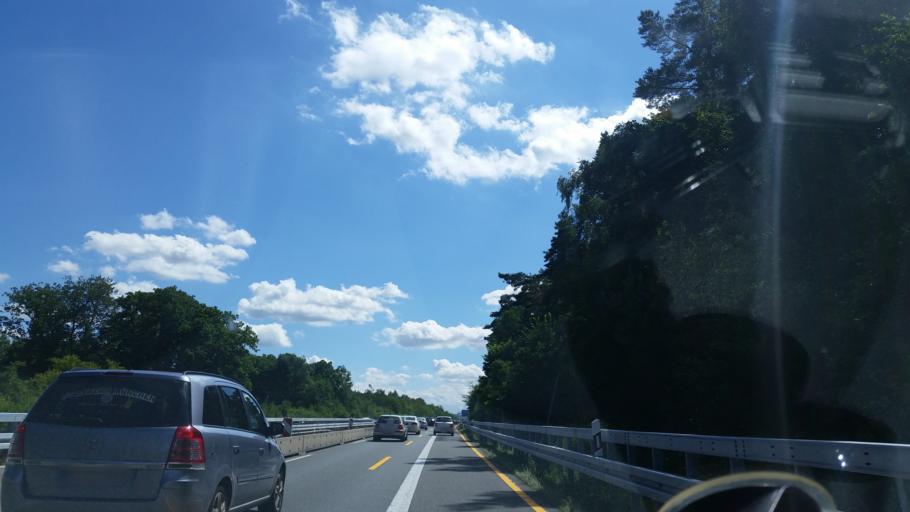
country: DE
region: Lower Saxony
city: Lehre
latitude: 52.3288
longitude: 10.7337
